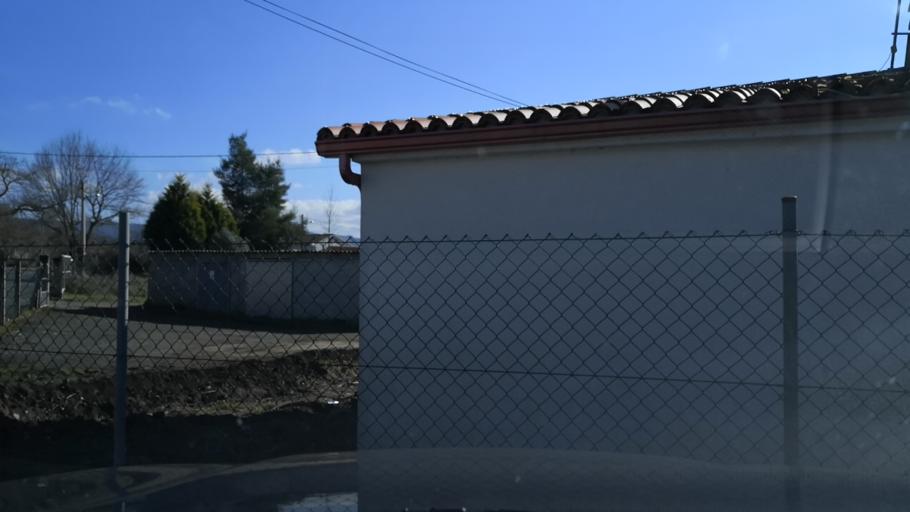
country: ES
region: Galicia
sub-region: Provincia da Coruna
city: Ribeira
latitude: 42.7141
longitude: -8.4464
